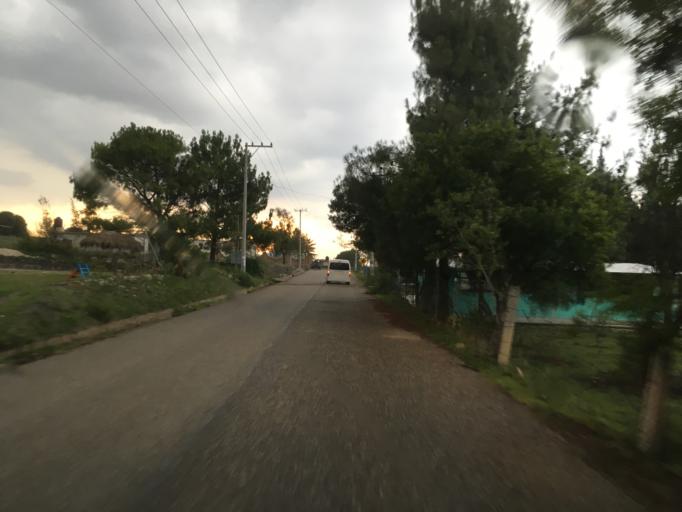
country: MX
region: Oaxaca
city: Santiago Tilantongo
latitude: 17.2885
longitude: -97.2844
